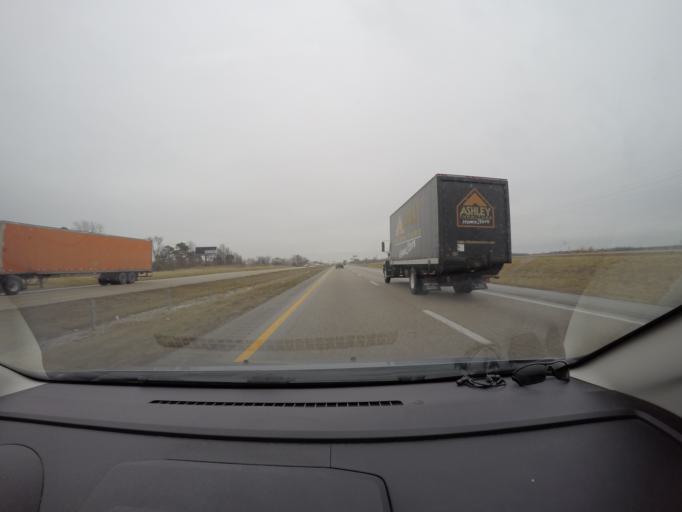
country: US
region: Missouri
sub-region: Montgomery County
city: Montgomery City
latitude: 38.9032
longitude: -91.4815
